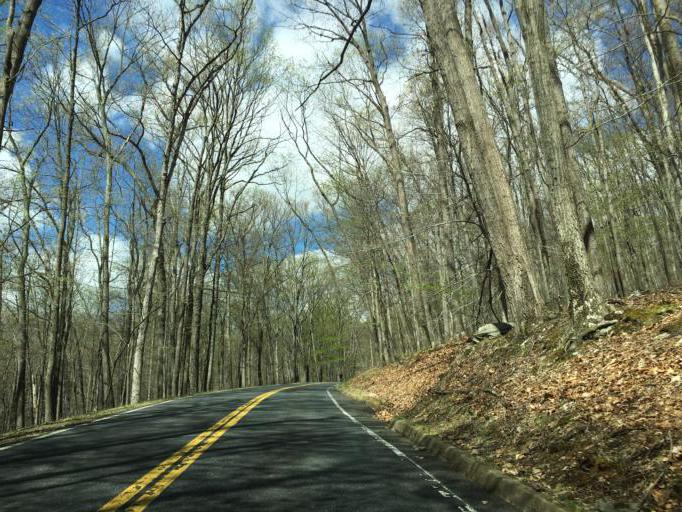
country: US
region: Maryland
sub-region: Frederick County
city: Thurmont
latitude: 39.6387
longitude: -77.4472
